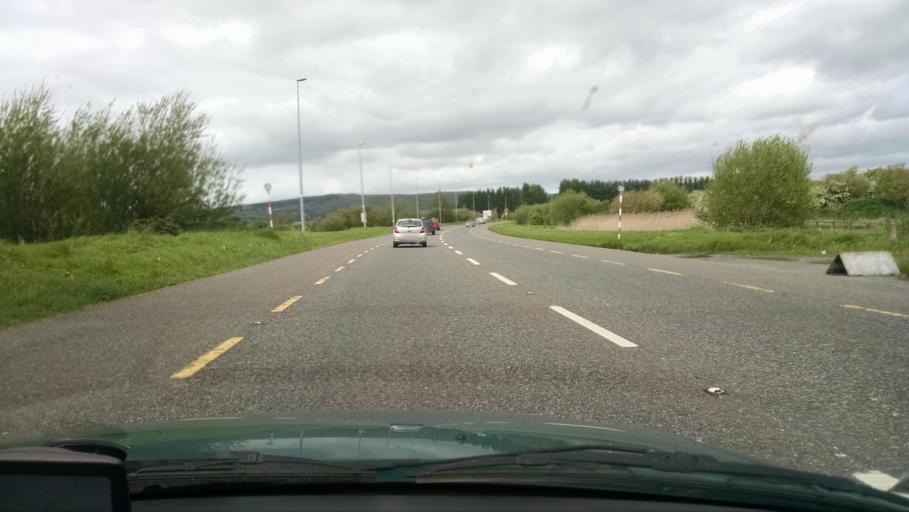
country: IE
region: Munster
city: Moyross
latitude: 52.6695
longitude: -8.6746
